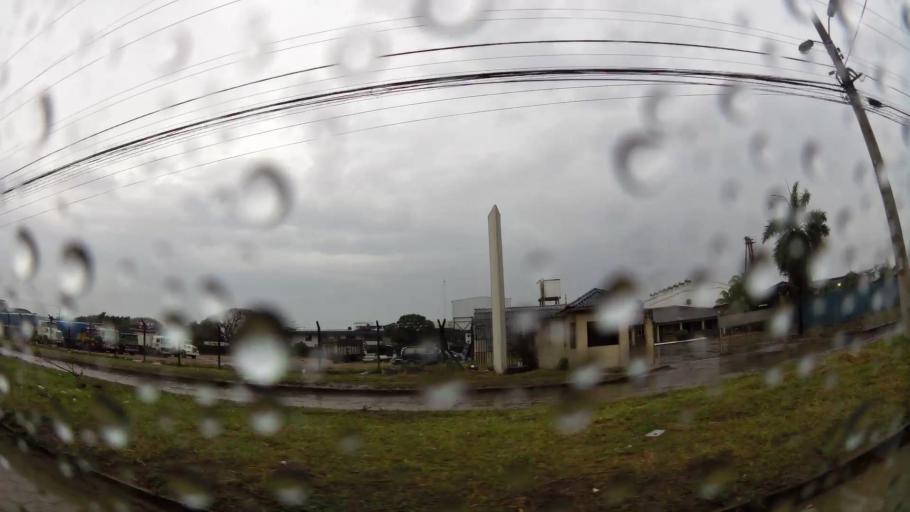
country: BO
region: Santa Cruz
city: Santa Cruz de la Sierra
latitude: -17.7607
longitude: -63.1398
